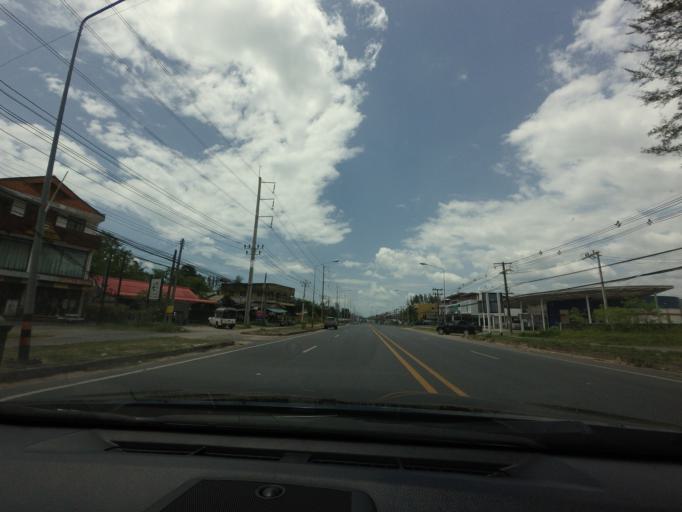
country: TH
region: Phangnga
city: Ban Khao Lak
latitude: 8.6615
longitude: 98.2533
